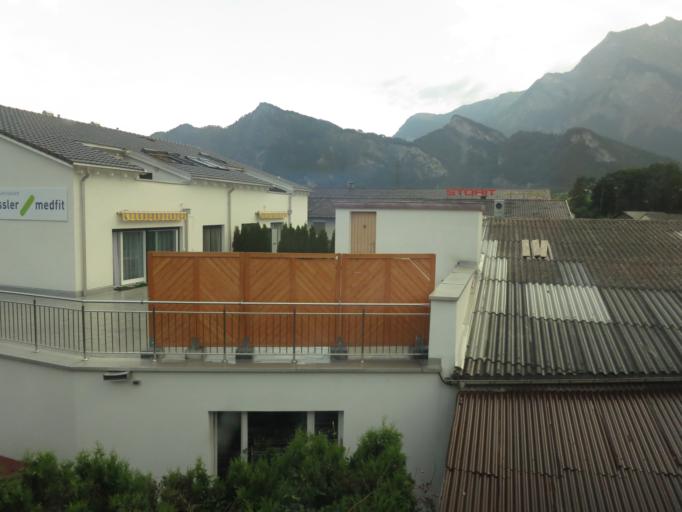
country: CH
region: Saint Gallen
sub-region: Wahlkreis Sarganserland
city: Bad Ragaz
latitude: 47.0104
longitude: 9.5065
